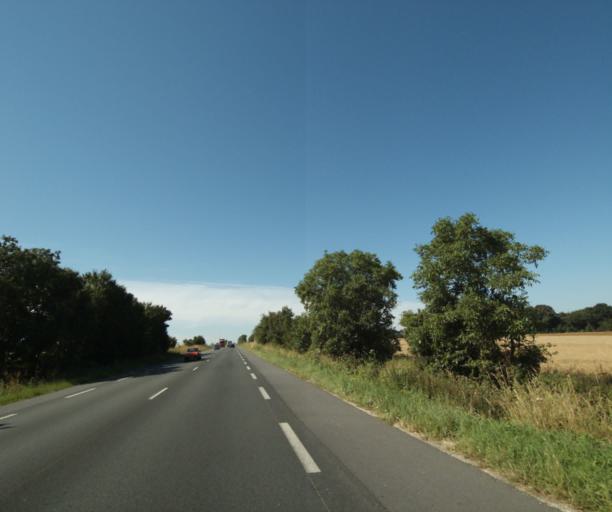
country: FR
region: Pays de la Loire
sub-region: Departement de la Mayenne
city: Bonchamp-les-Laval
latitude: 48.0664
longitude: -0.7325
